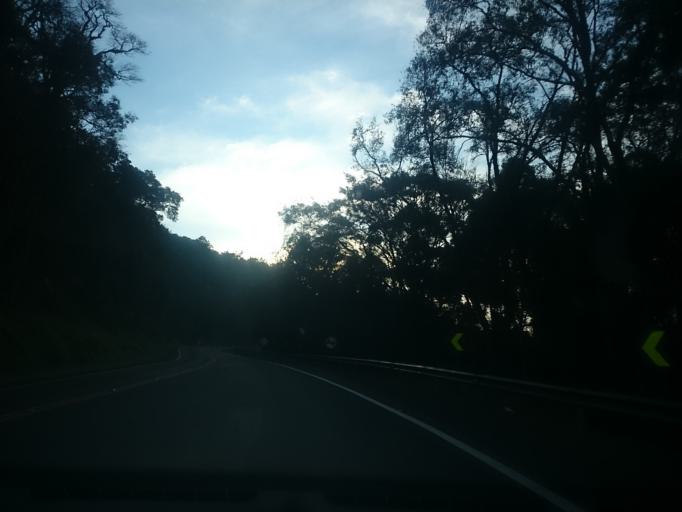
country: BR
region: Rio Grande do Sul
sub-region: Vacaria
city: Estrela
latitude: -28.1994
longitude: -50.7268
